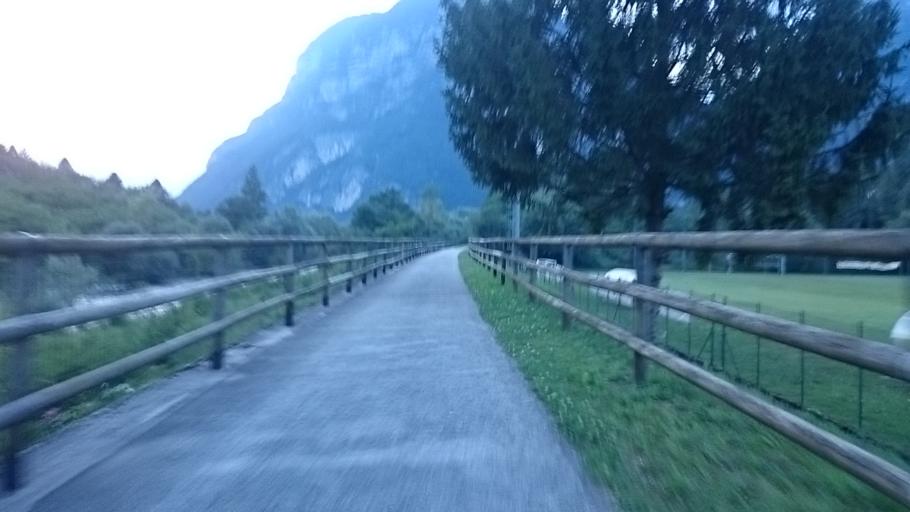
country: IT
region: Trentino-Alto Adige
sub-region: Provincia di Trento
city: Grigno
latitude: 46.0071
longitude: 11.6407
